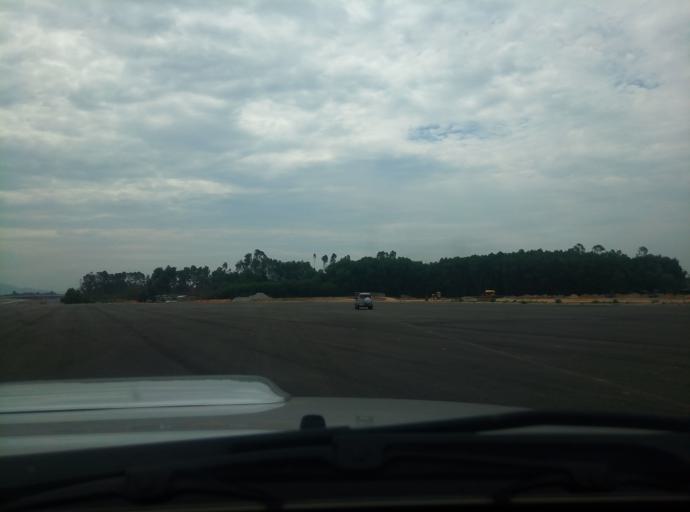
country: VN
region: Quang Nam
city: Tam Ky
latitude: 15.5290
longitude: 108.4780
